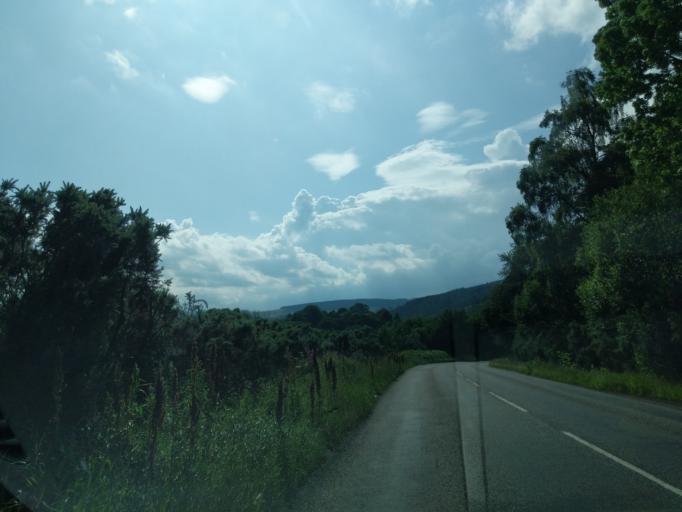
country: GB
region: Scotland
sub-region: Moray
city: Rothes
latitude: 57.5426
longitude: -3.1803
